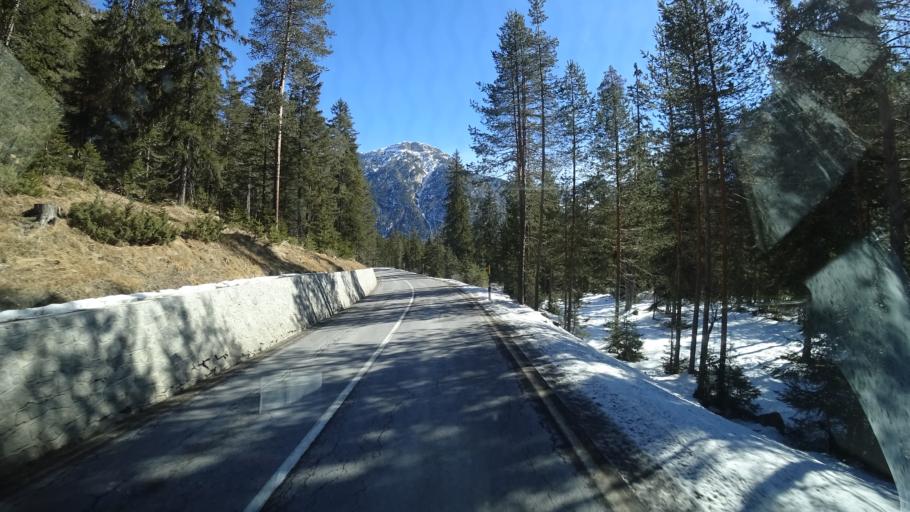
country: IT
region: Veneto
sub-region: Provincia di Belluno
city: Cortina d'Ampezzo
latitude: 46.6221
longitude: 12.2039
